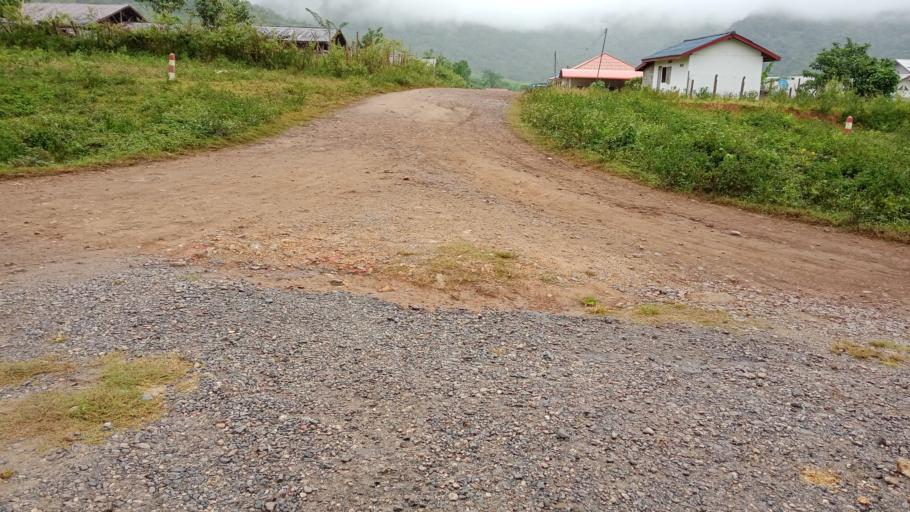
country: LA
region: Xiangkhoang
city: Phonsavan
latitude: 19.1069
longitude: 102.9245
